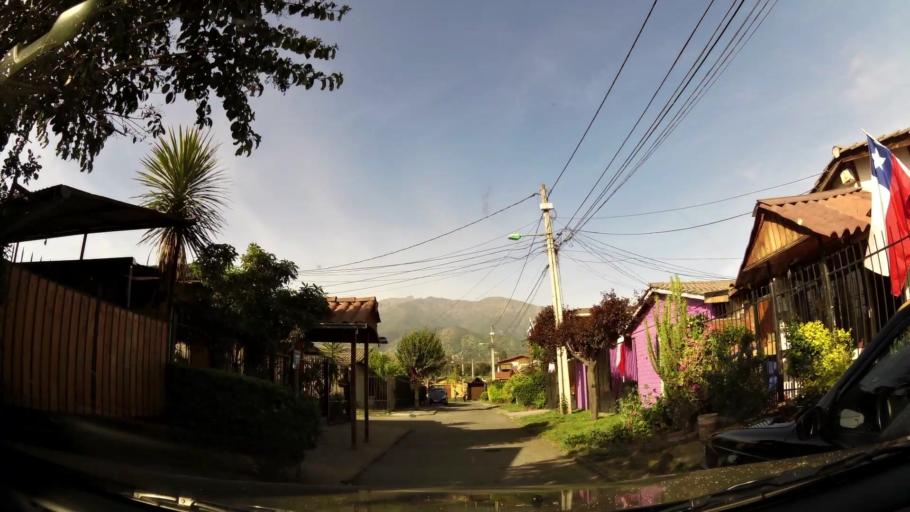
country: CL
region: Santiago Metropolitan
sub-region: Provincia de Cordillera
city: Puente Alto
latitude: -33.5757
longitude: -70.5552
